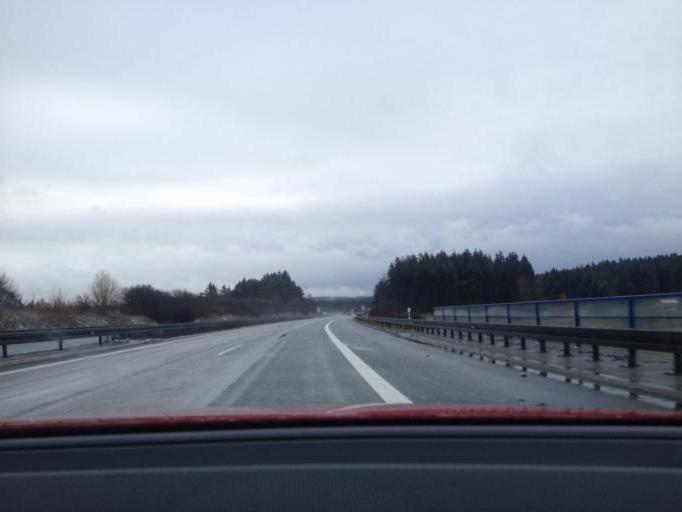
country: DE
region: Bavaria
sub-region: Upper Franconia
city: Schonwald
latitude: 50.1988
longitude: 12.1024
